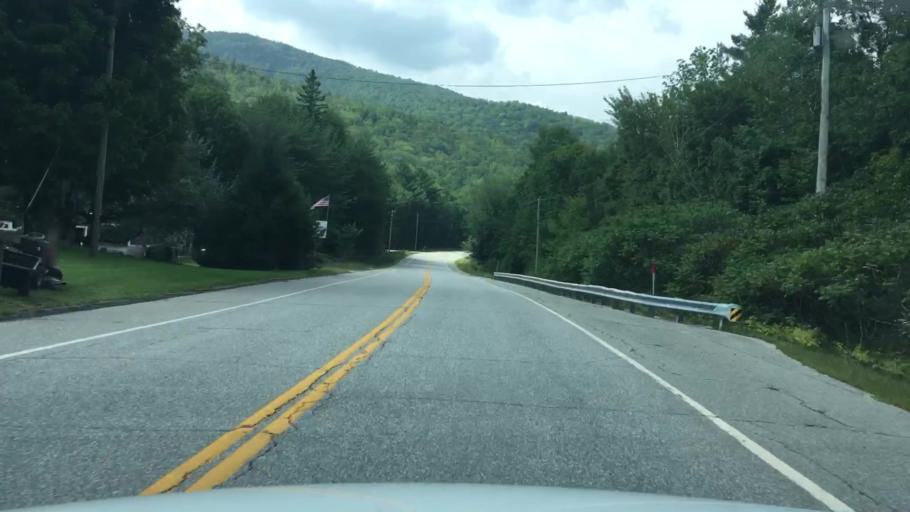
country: US
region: Maine
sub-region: Oxford County
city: Rumford
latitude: 44.5484
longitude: -70.7028
